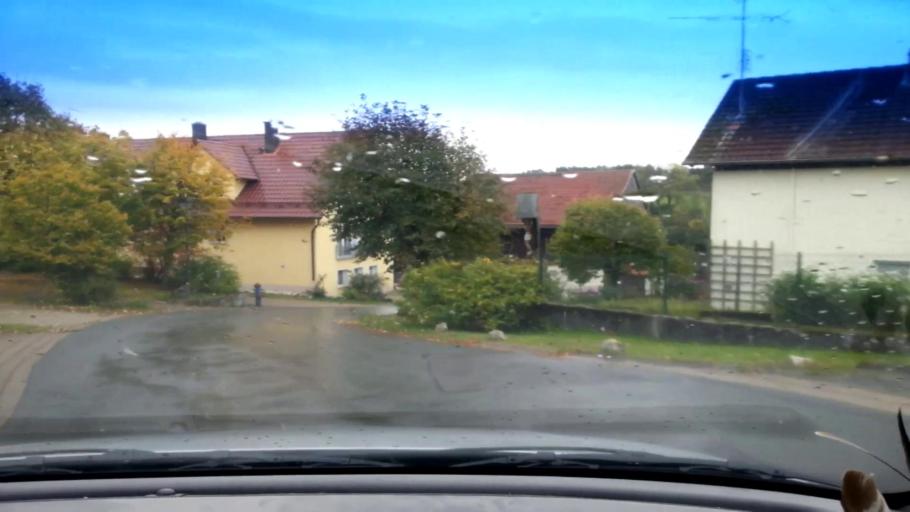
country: DE
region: Bavaria
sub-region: Upper Franconia
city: Poxdorf
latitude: 49.8891
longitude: 11.1110
